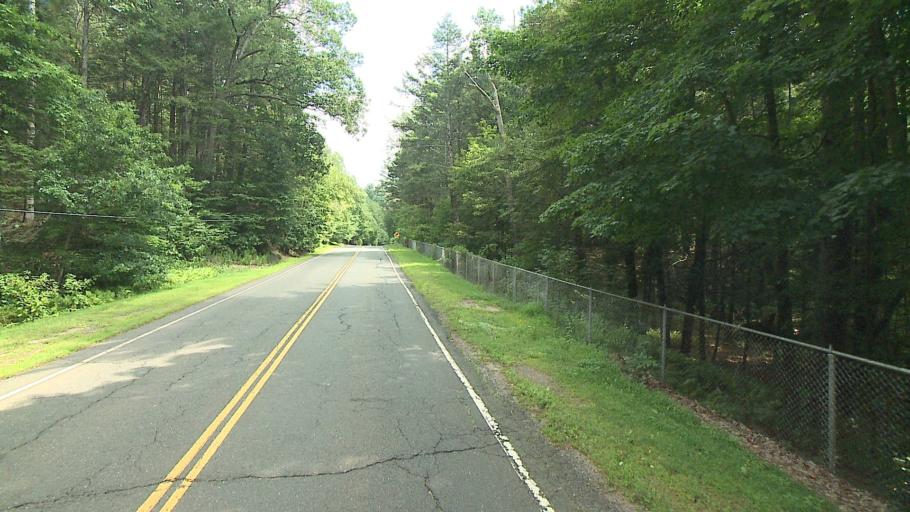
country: US
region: Connecticut
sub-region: Litchfield County
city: Thomaston
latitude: 41.6699
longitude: -73.1367
